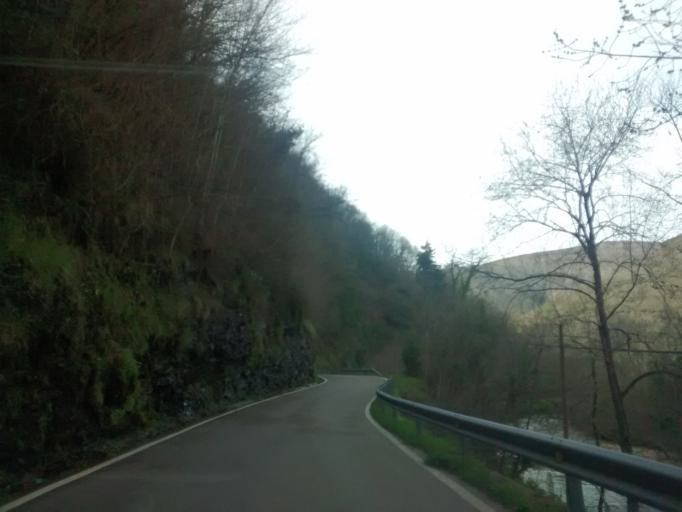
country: ES
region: Cantabria
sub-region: Provincia de Cantabria
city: San Pedro del Romeral
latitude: 43.1674
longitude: -3.8601
